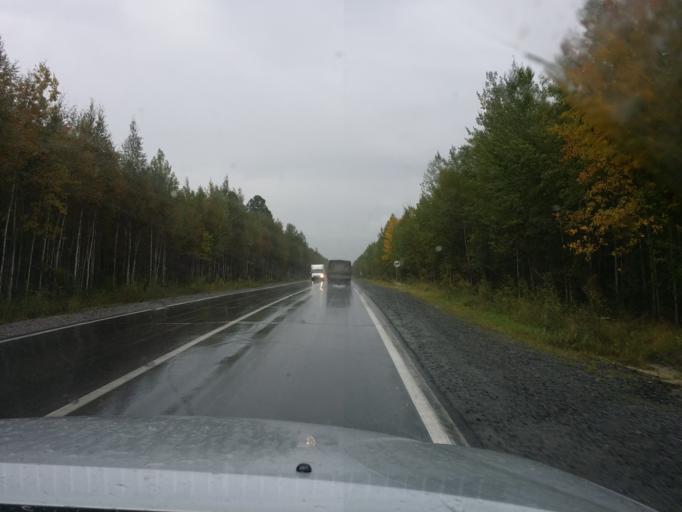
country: RU
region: Khanty-Mansiyskiy Avtonomnyy Okrug
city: Langepas
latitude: 61.1591
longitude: 75.6356
